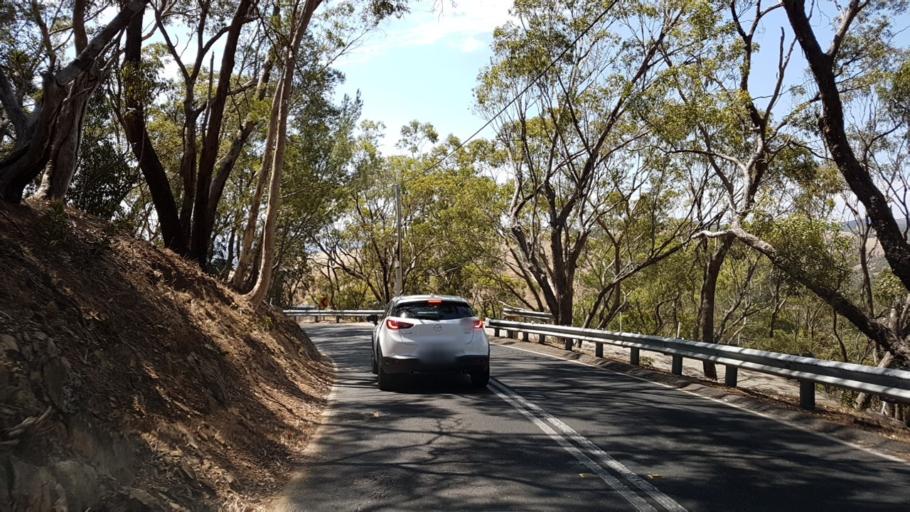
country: AU
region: South Australia
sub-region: Mitcham
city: Belair
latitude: -34.9956
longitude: 138.6296
